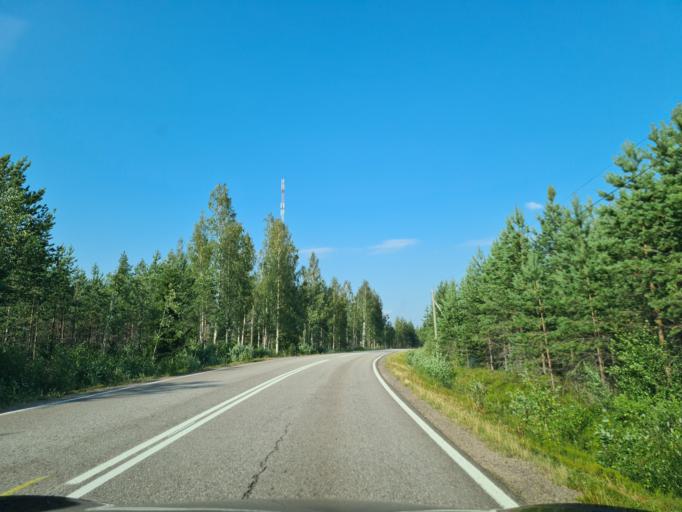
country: FI
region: Satakunta
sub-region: Pohjois-Satakunta
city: Karvia
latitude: 62.3217
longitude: 22.6712
